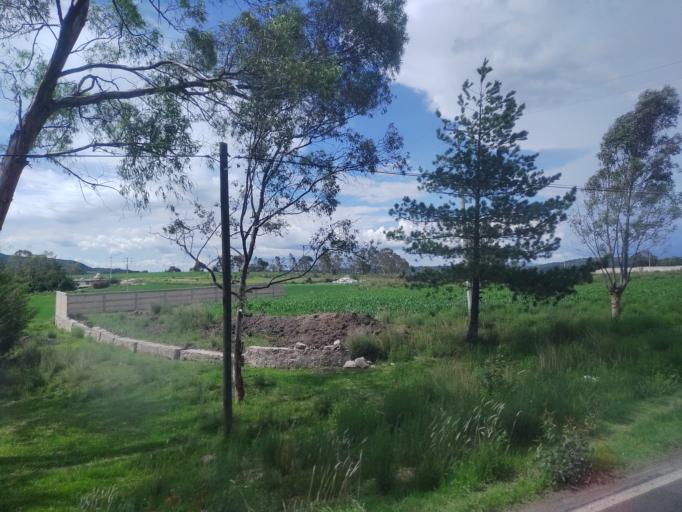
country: MX
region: Mexico
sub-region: Aculco
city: El Colorado
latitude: 20.0980
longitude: -99.7435
